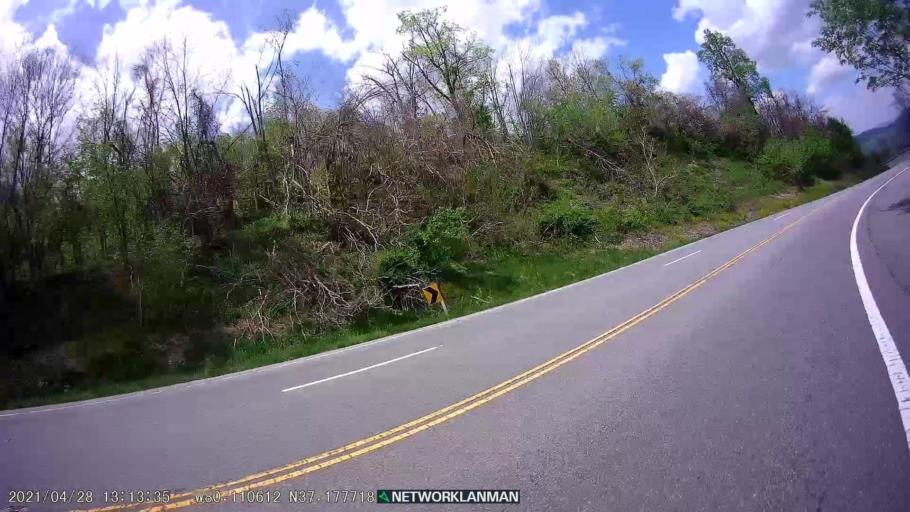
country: US
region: Virginia
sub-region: Roanoke County
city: Cave Spring
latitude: 37.1781
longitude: -80.1105
